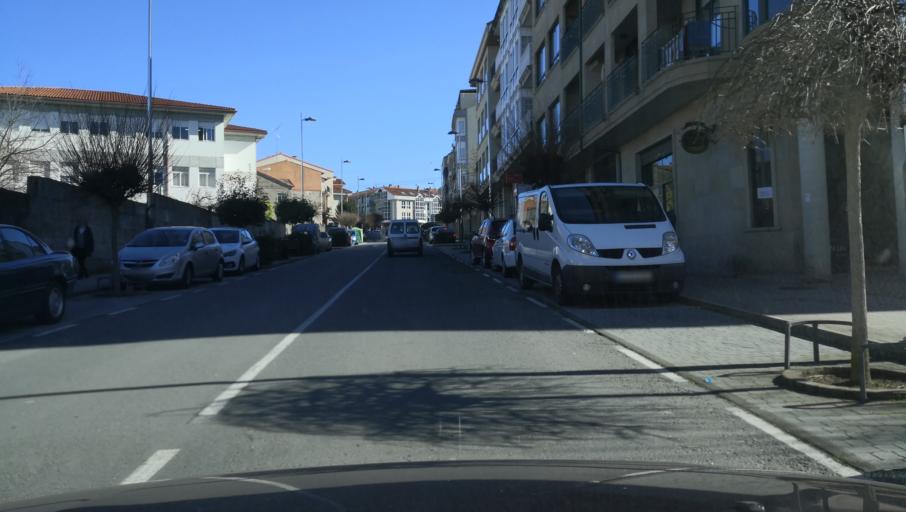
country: ES
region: Galicia
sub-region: Provincia de Ourense
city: Allariz
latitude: 42.1879
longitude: -7.8015
